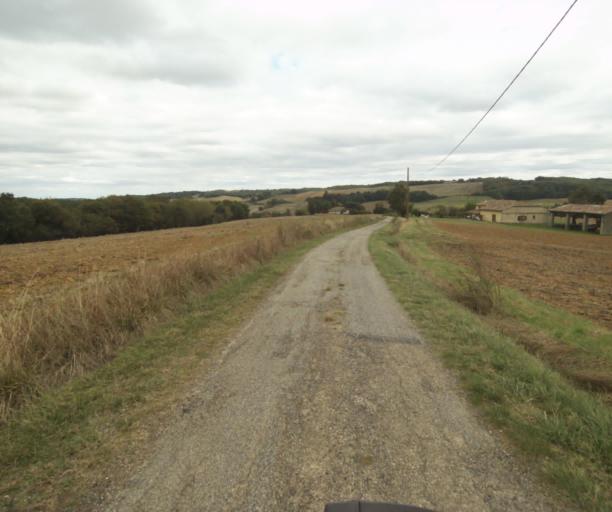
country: FR
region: Midi-Pyrenees
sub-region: Departement du Tarn-et-Garonne
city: Beaumont-de-Lomagne
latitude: 43.8489
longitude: 1.0695
